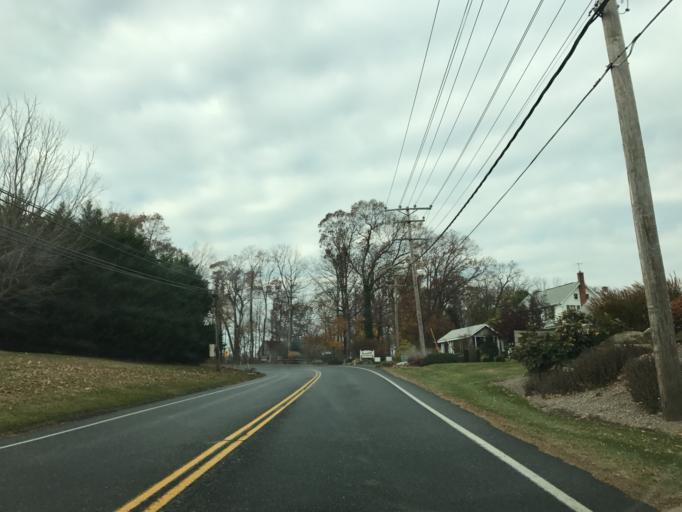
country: US
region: Maryland
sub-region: Harford County
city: Jarrettsville
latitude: 39.6090
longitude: -76.4577
